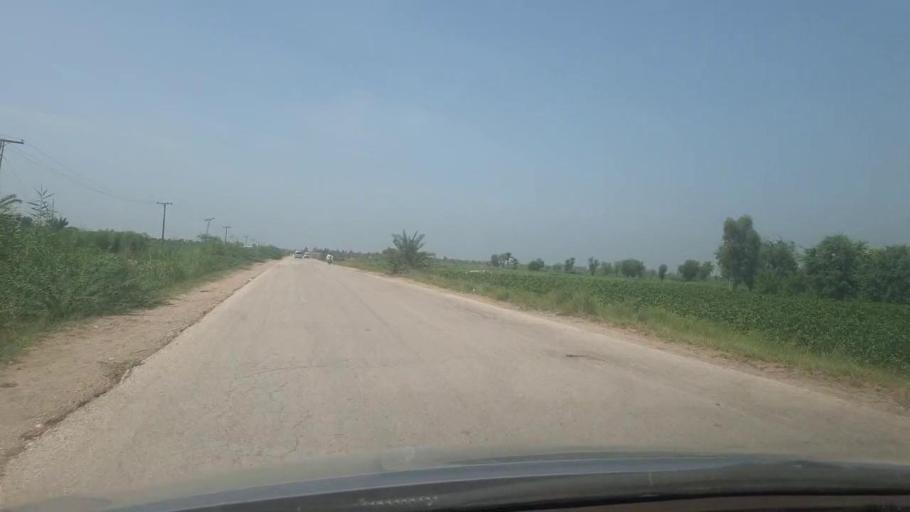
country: PK
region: Sindh
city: Ranipur
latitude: 27.2665
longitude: 68.5928
